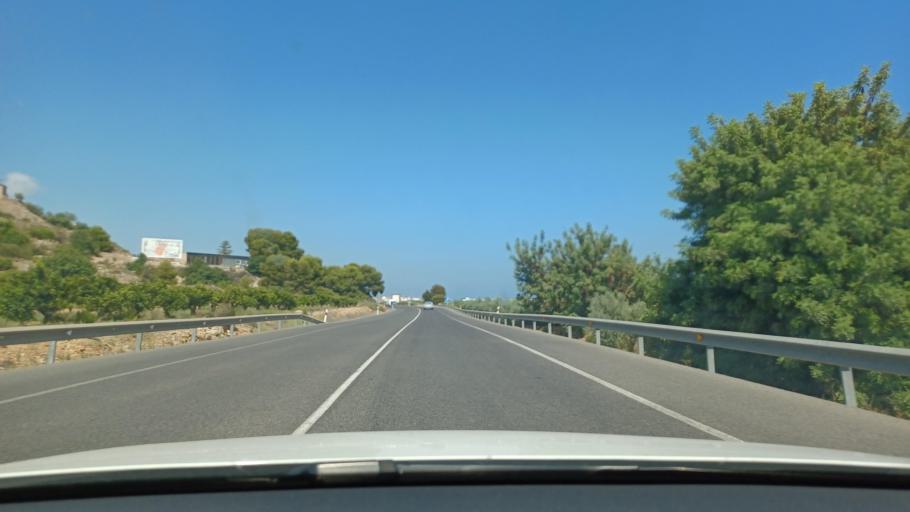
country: ES
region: Valencia
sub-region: Provincia de Castello
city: Chilches
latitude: 39.7757
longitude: -0.2006
